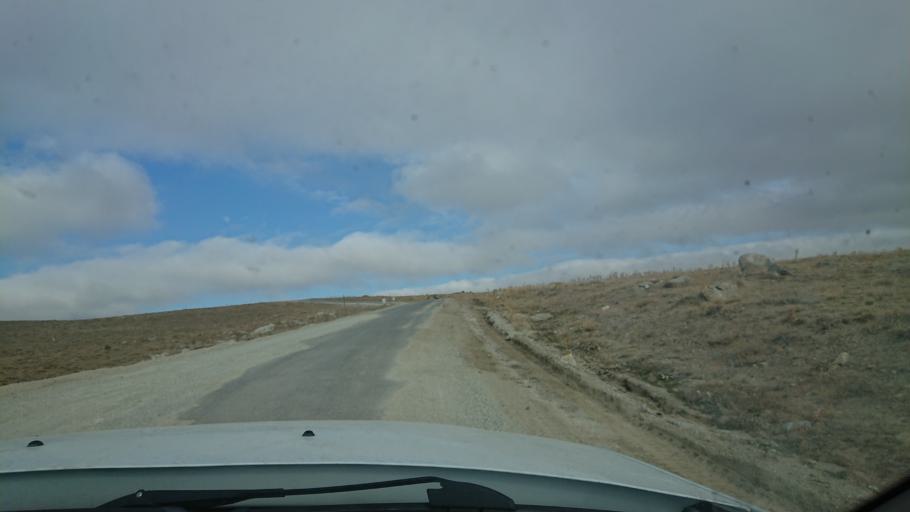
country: TR
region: Aksaray
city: Ortakoy
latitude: 38.7751
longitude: 34.0108
